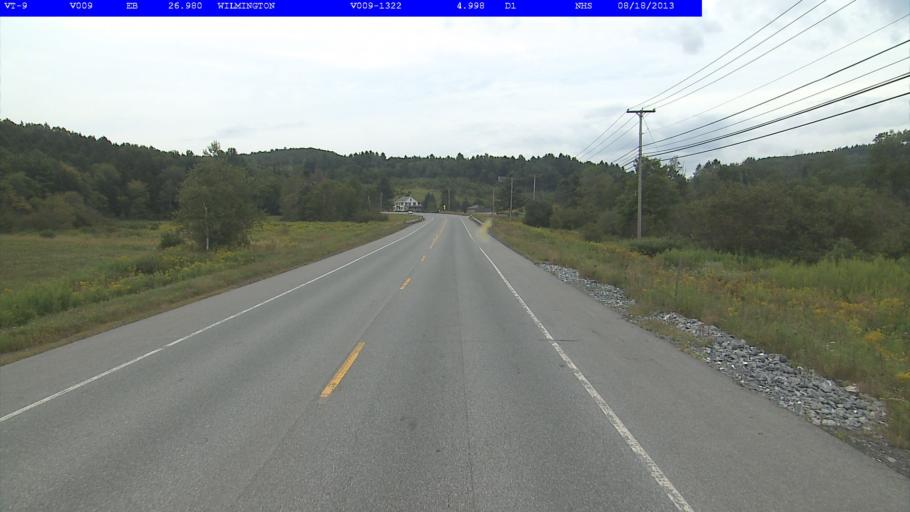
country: US
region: Vermont
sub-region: Windham County
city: Dover
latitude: 42.8564
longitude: -72.8388
